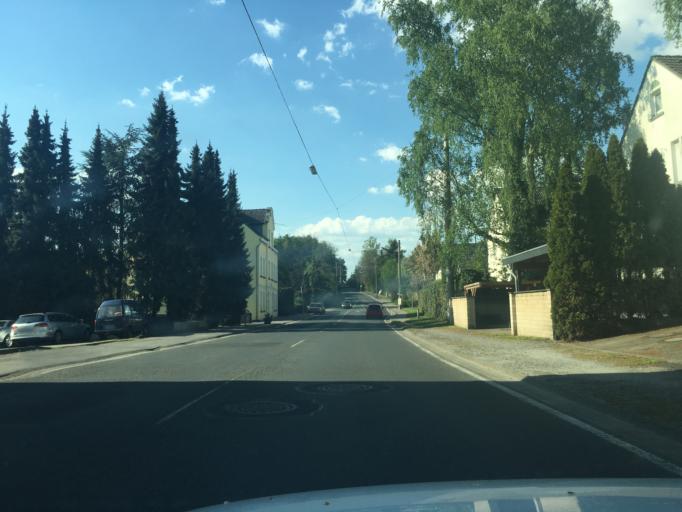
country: DE
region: North Rhine-Westphalia
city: Haan
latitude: 51.1786
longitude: 6.9873
